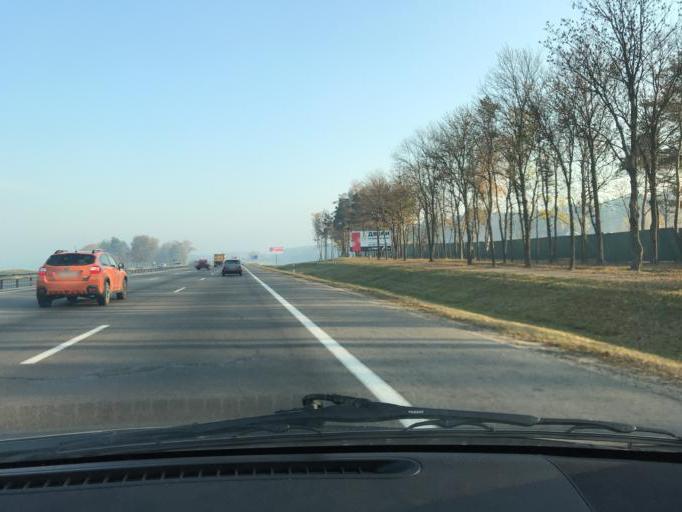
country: BY
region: Minsk
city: Borovlyany
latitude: 53.9712
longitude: 27.6478
